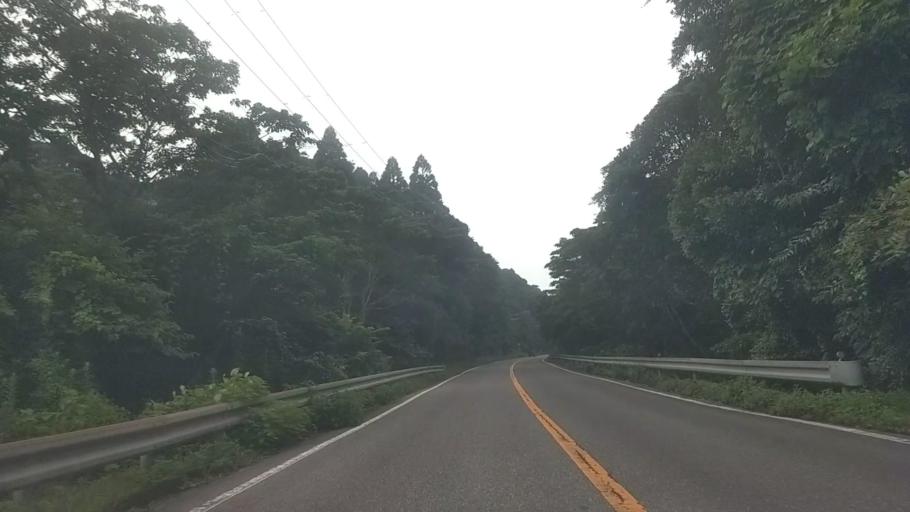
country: JP
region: Chiba
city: Katsuura
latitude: 35.1633
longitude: 140.3203
